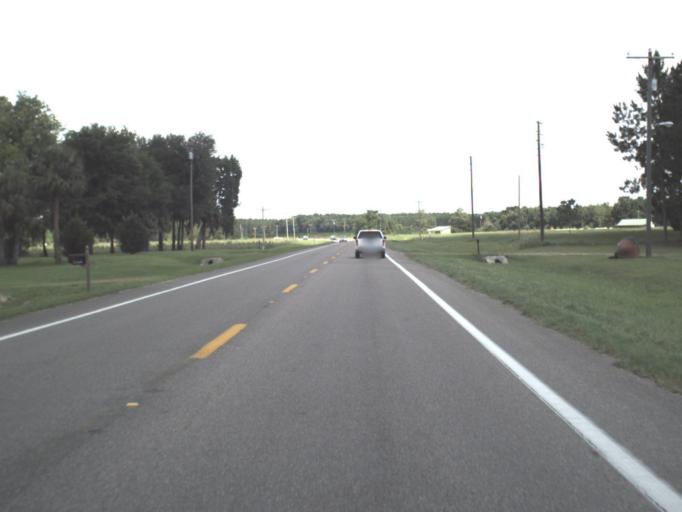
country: US
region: Florida
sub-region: Lafayette County
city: Mayo
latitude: 29.9556
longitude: -82.9617
